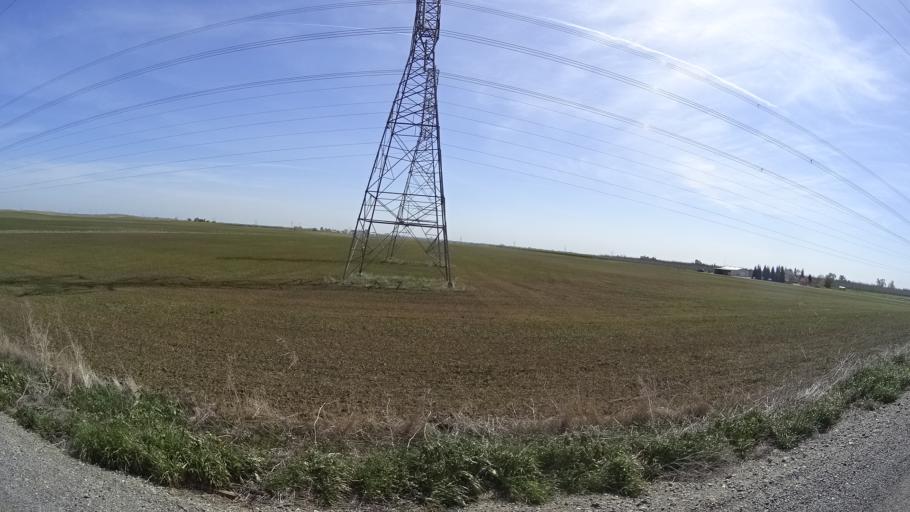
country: US
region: California
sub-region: Glenn County
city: Willows
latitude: 39.5335
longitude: -122.2869
